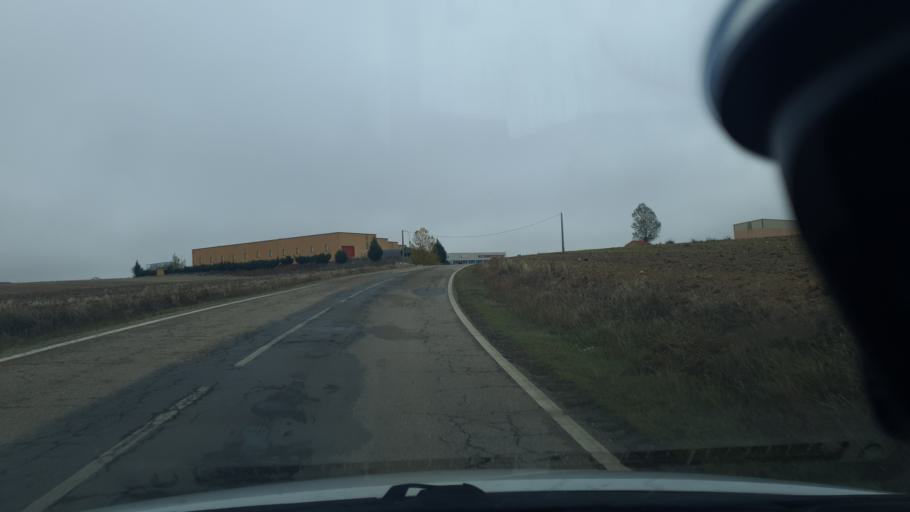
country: ES
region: Castille and Leon
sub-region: Provincia de Segovia
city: Valseca
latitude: 41.0041
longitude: -4.1620
